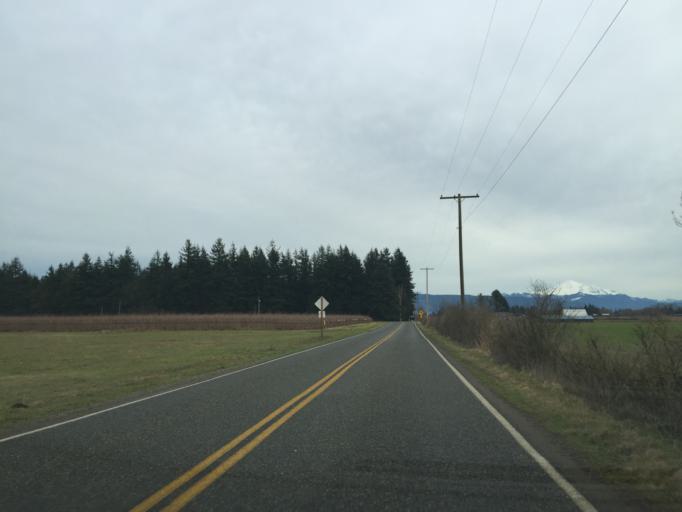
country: US
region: Washington
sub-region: Whatcom County
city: Lynden
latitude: 48.9024
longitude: -122.5171
